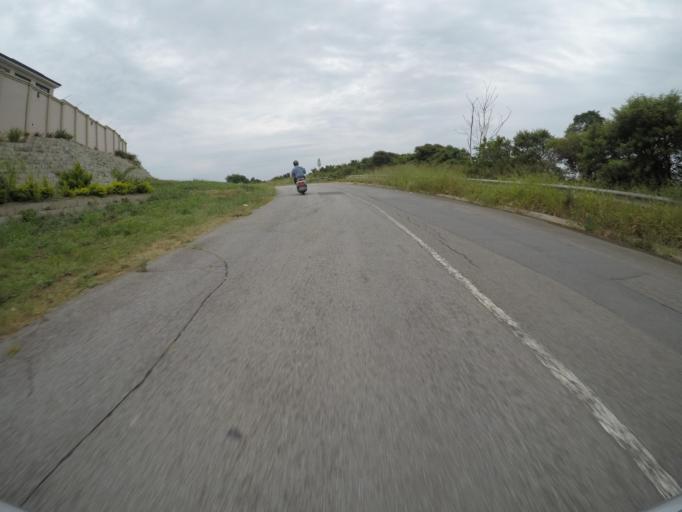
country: ZA
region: Eastern Cape
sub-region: Buffalo City Metropolitan Municipality
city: East London
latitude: -32.9532
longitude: 27.8990
